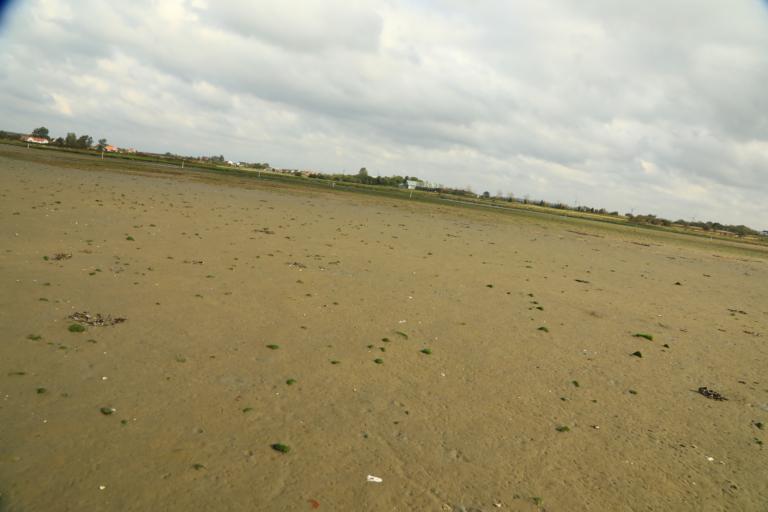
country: SE
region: Halland
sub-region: Varbergs Kommun
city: Traslovslage
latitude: 57.0213
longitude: 12.3280
